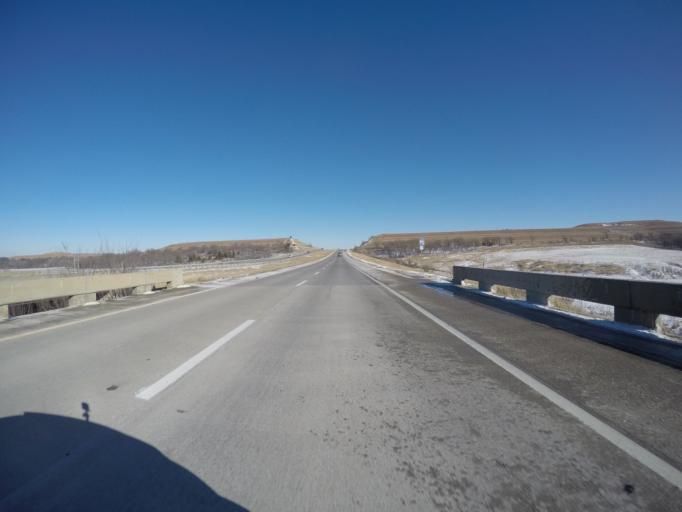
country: US
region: Kansas
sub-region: Riley County
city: Manhattan
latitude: 39.0672
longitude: -96.4979
